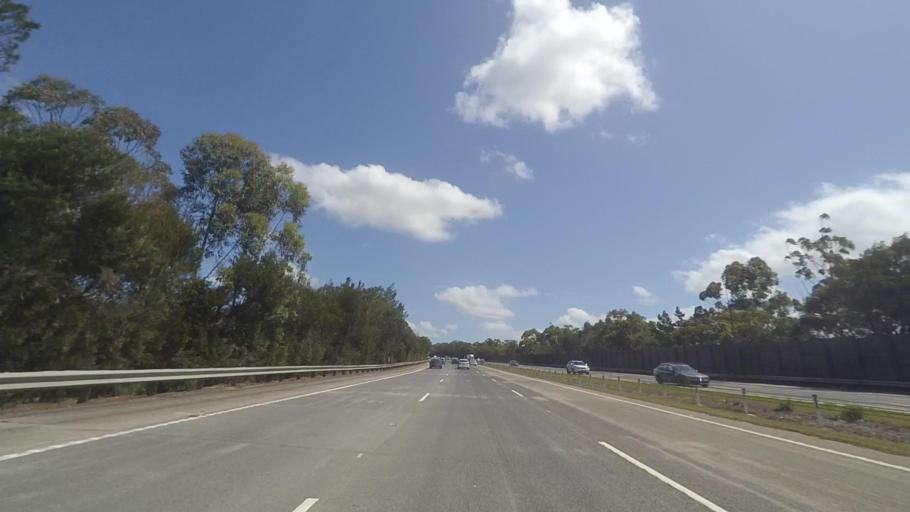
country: AU
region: New South Wales
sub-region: Hornsby Shire
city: Mount Colah
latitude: -33.6710
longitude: 151.1207
